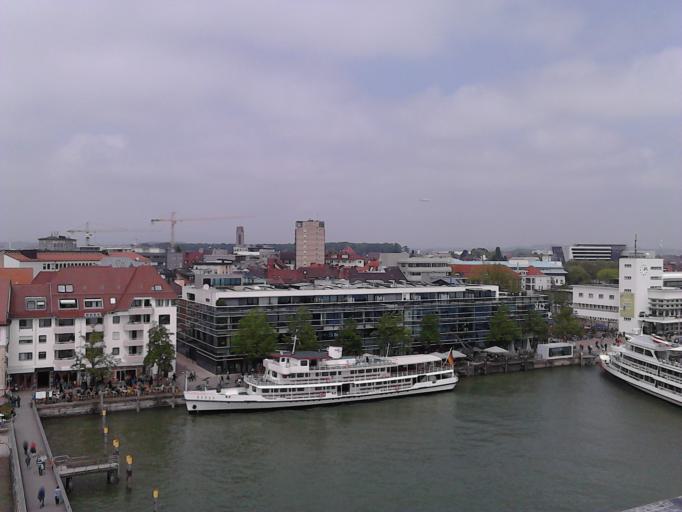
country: DE
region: Baden-Wuerttemberg
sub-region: Tuebingen Region
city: Friedrichshafen
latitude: 47.6486
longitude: 9.4821
